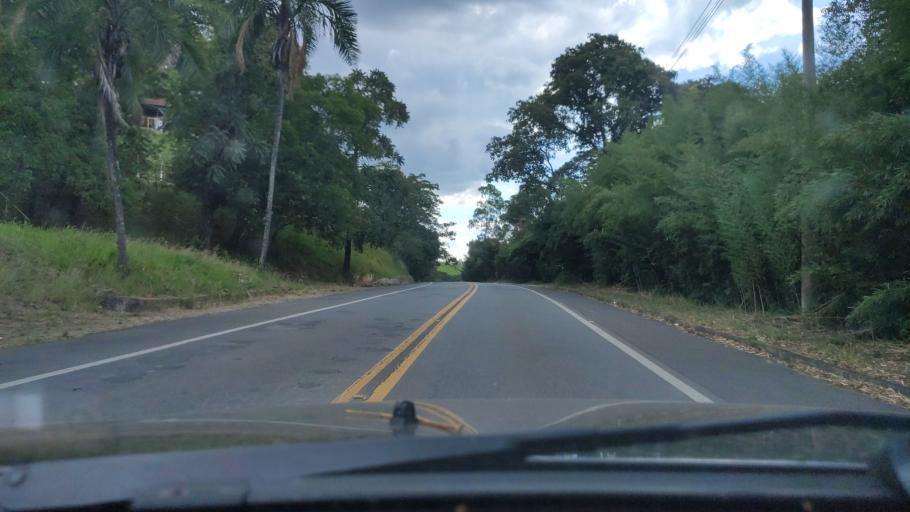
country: BR
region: Sao Paulo
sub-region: Aguas De Lindoia
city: Aguas de Lindoia
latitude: -22.4716
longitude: -46.7126
